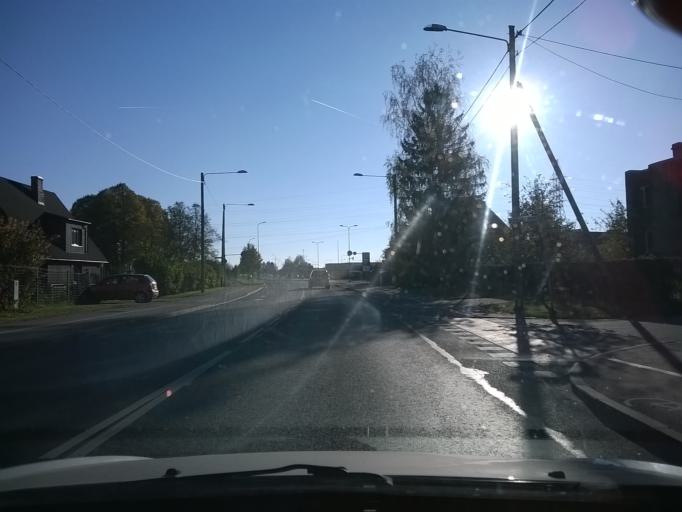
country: EE
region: Tartu
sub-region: UElenurme vald
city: Ulenurme
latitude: 58.3475
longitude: 26.7157
